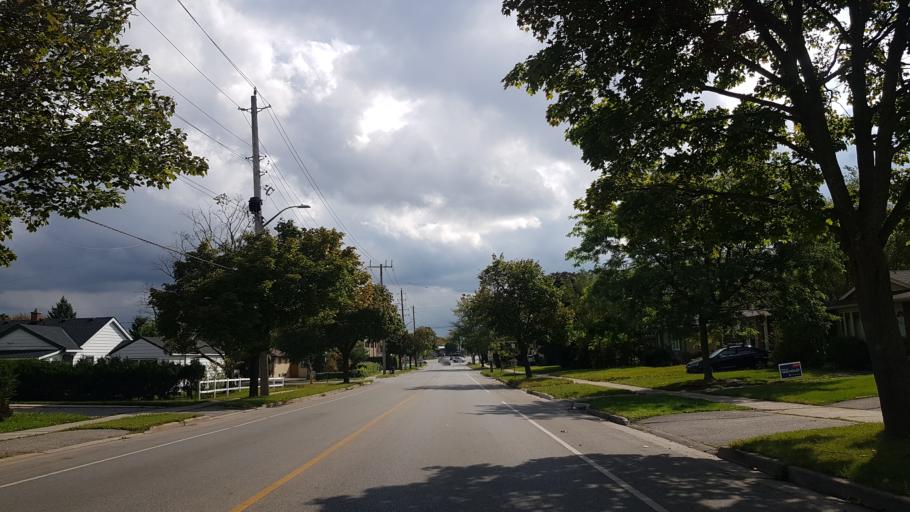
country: CA
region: Ontario
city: London
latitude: 42.9445
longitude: -81.2375
